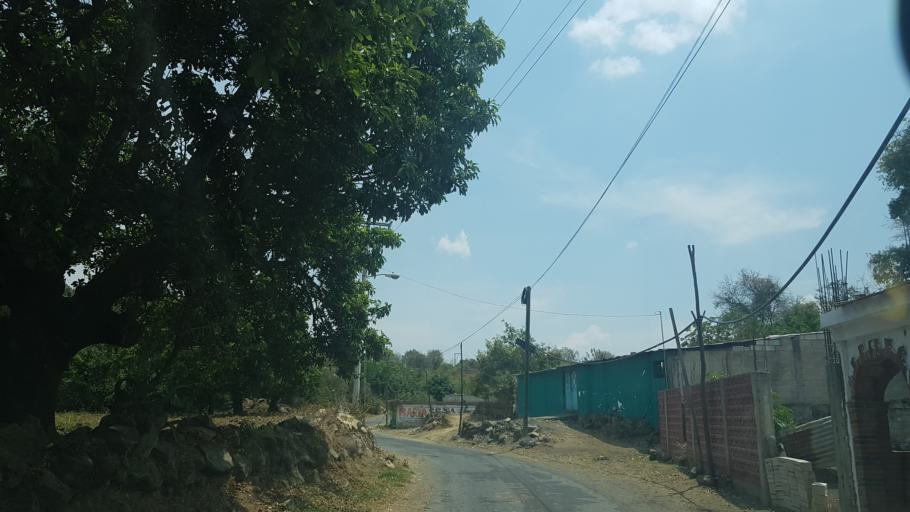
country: MX
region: Puebla
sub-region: Tochimilco
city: La Magdalena Yancuitlalpan
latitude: 18.8872
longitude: -98.6067
